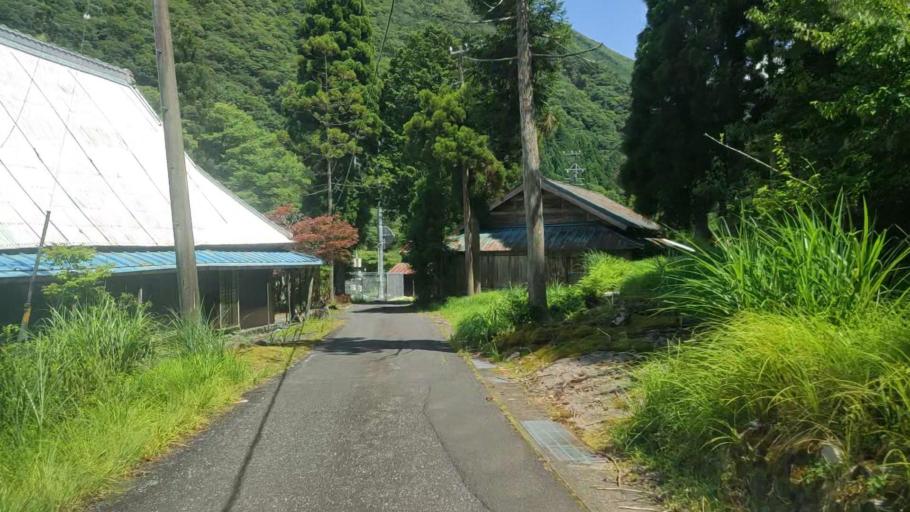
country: JP
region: Gifu
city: Godo
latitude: 35.7071
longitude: 136.5862
